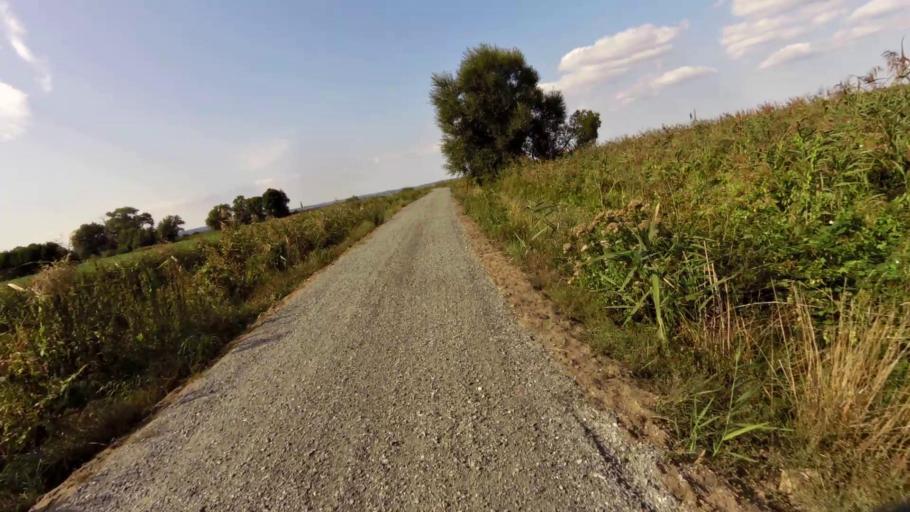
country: PL
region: West Pomeranian Voivodeship
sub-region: Szczecin
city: Szczecin
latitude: 53.4338
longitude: 14.6965
